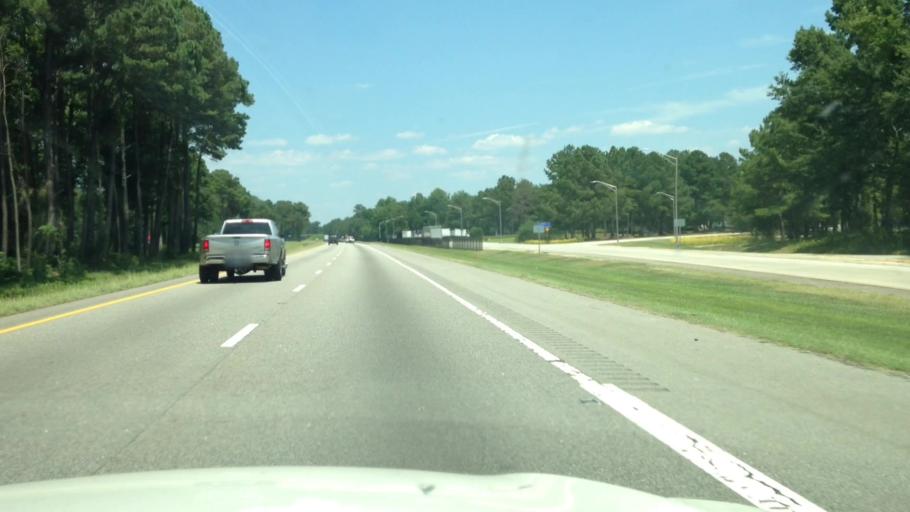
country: US
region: North Carolina
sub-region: Robeson County
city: Rowland
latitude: 34.5381
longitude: -79.2384
